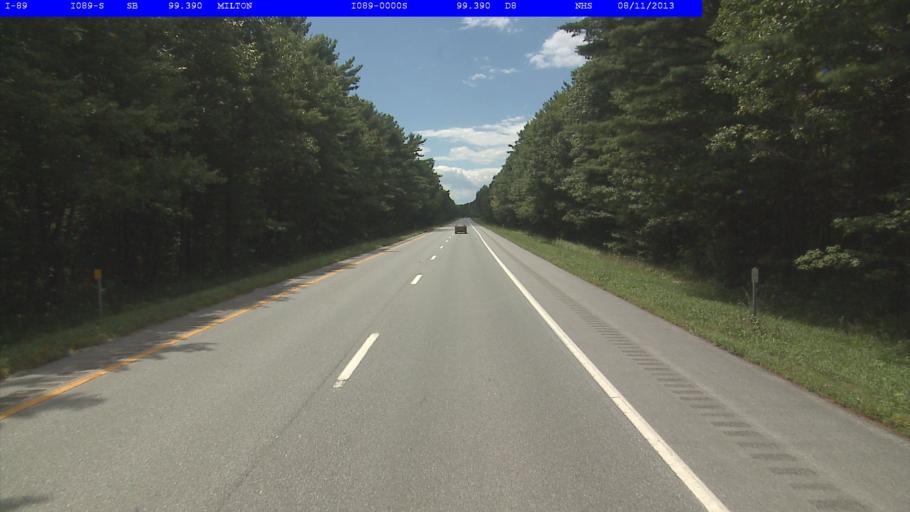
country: US
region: Vermont
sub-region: Chittenden County
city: Milton
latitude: 44.6107
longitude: -73.1661
